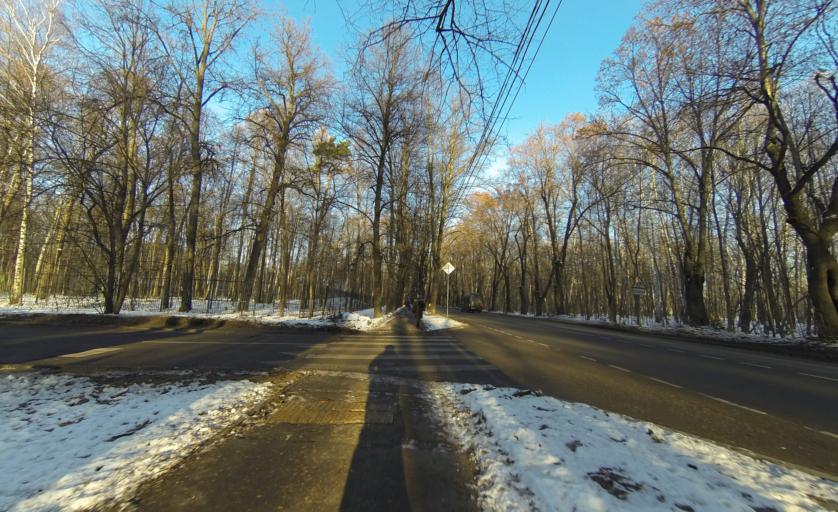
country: RU
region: Moscow
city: Sokol'niki
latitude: 55.8111
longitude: 37.6830
